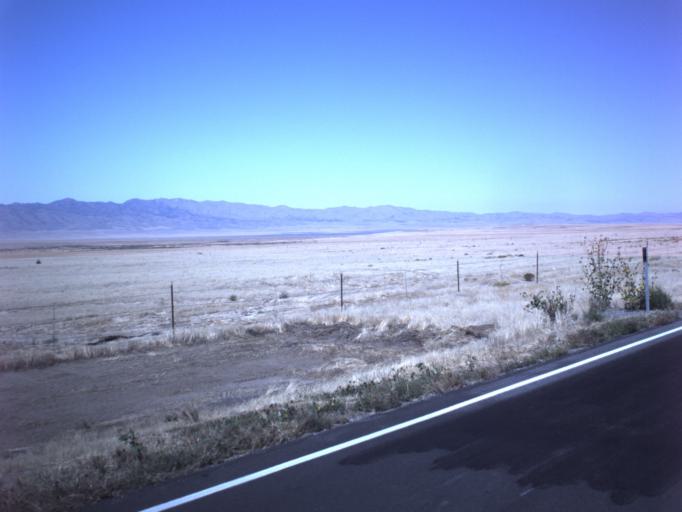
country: US
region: Utah
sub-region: Tooele County
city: Grantsville
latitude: 40.3974
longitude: -112.7477
